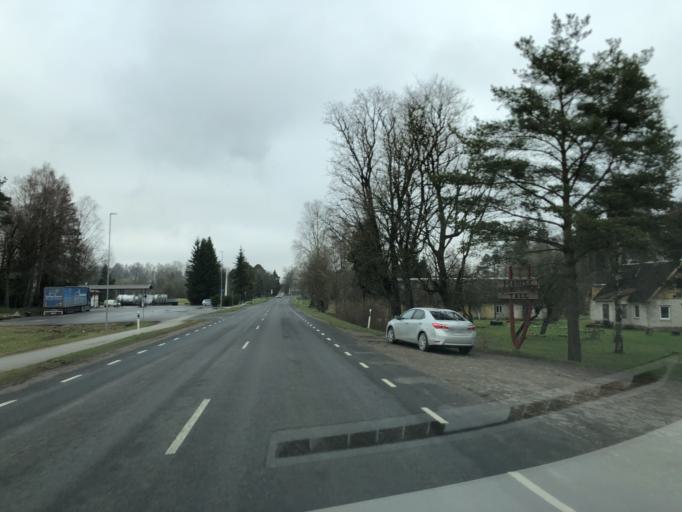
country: EE
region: Laeaene-Virumaa
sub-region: Vaeike-Maarja vald
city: Vaike-Maarja
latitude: 59.1099
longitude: 26.2363
